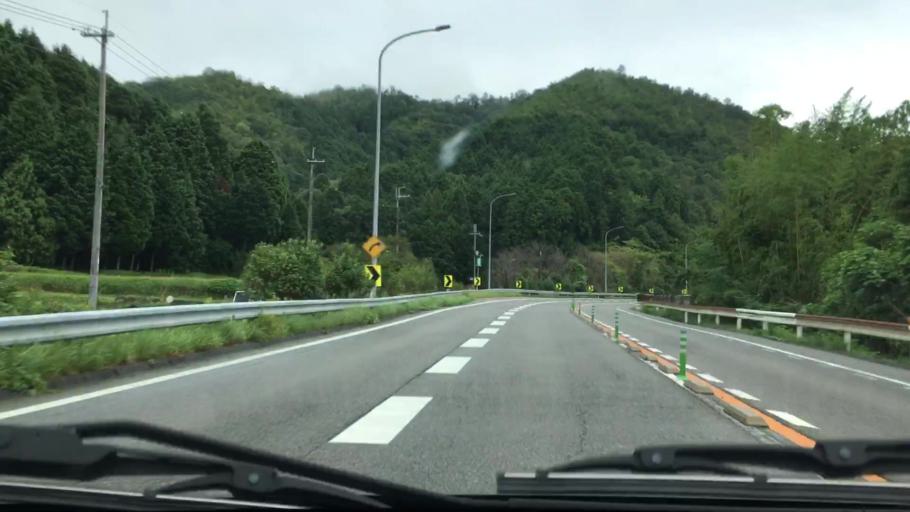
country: JP
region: Hyogo
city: Himeji
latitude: 35.0019
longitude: 134.7677
